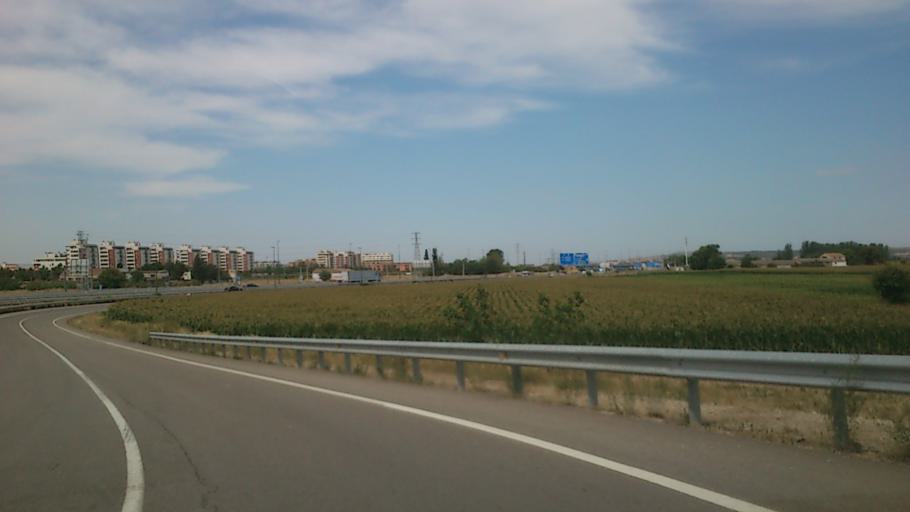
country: ES
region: Aragon
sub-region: Provincia de Zaragoza
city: Zaragoza
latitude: 41.6713
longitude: -0.8167
